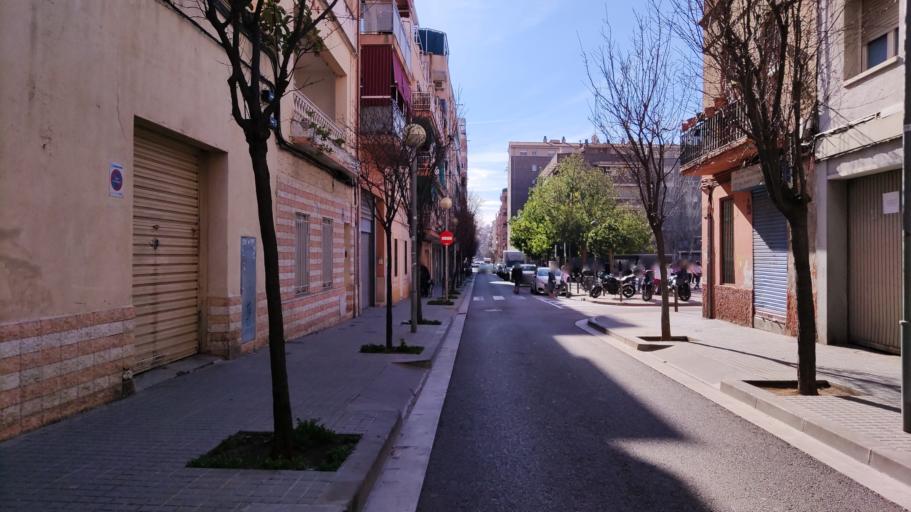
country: ES
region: Catalonia
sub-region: Provincia de Barcelona
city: Llefia
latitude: 41.4366
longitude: 2.2200
